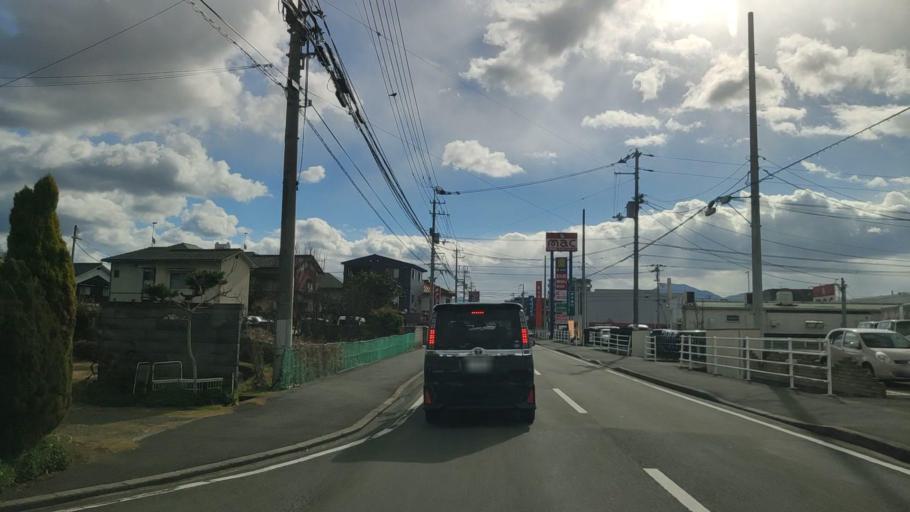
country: JP
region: Ehime
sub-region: Shikoku-chuo Shi
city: Matsuyama
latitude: 33.8109
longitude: 132.7953
